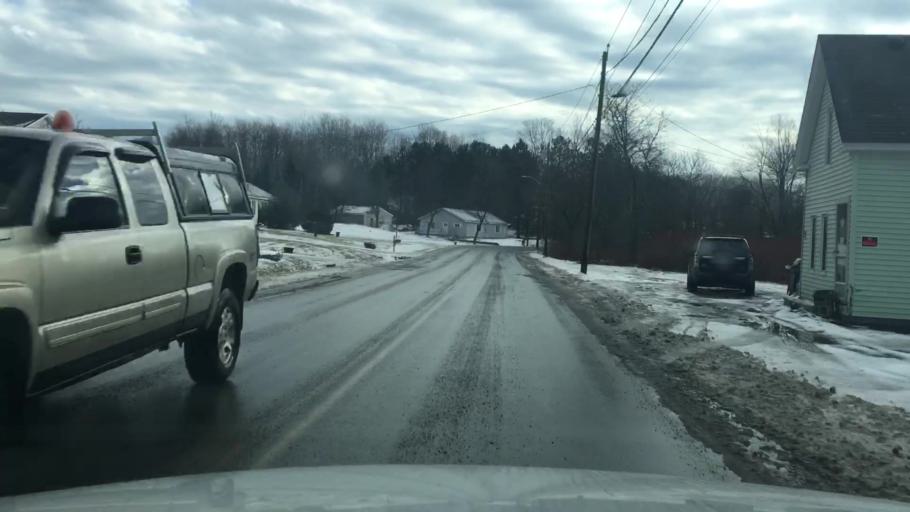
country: US
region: Maine
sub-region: Penobscot County
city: Brewer
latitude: 44.7651
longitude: -68.7785
